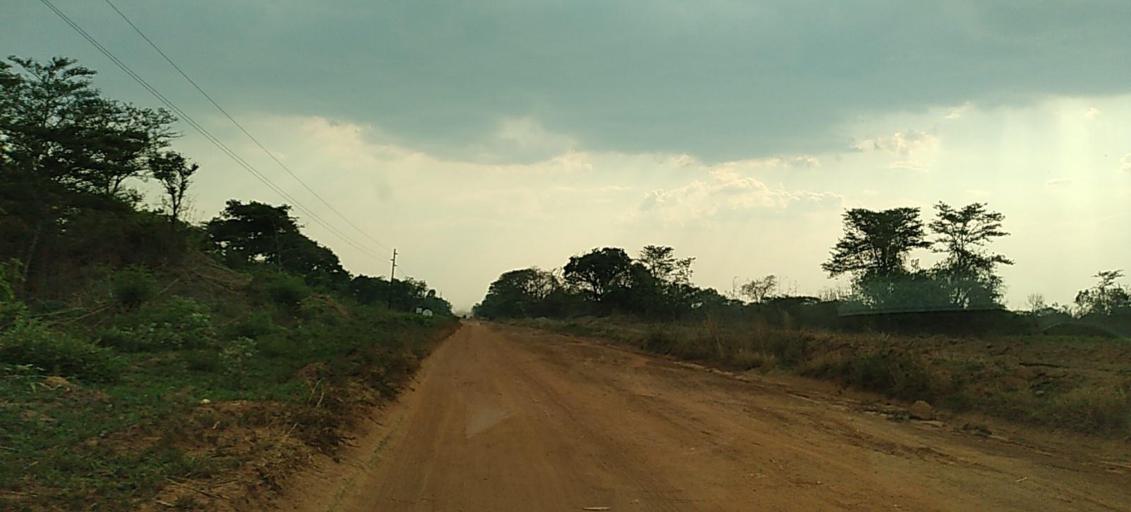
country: ZM
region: Copperbelt
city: Kalulushi
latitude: -12.9402
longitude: 27.9237
